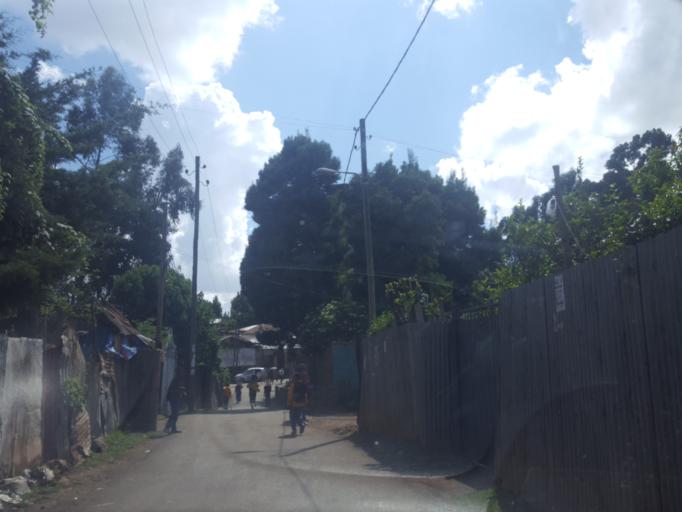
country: ET
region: Adis Abeba
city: Addis Ababa
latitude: 9.0623
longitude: 38.7636
